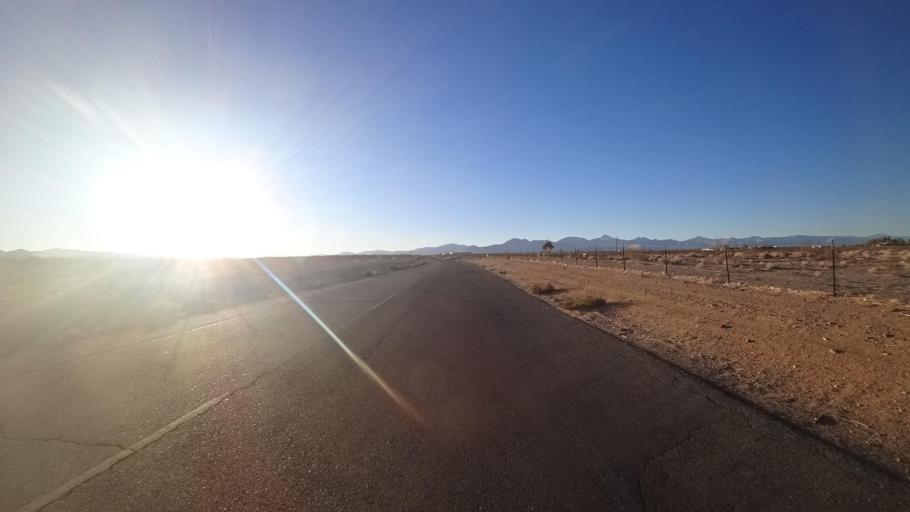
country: US
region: California
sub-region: Kern County
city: Ridgecrest
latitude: 35.6079
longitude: -117.7029
